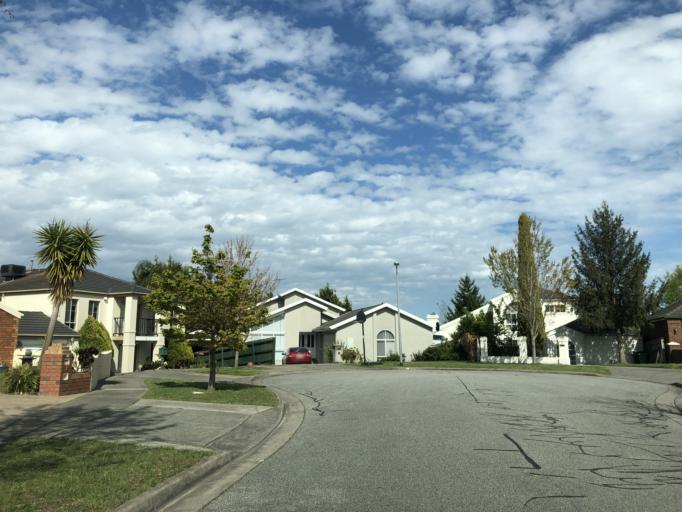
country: AU
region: Victoria
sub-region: Casey
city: Endeavour Hills
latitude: -37.9759
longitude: 145.2722
